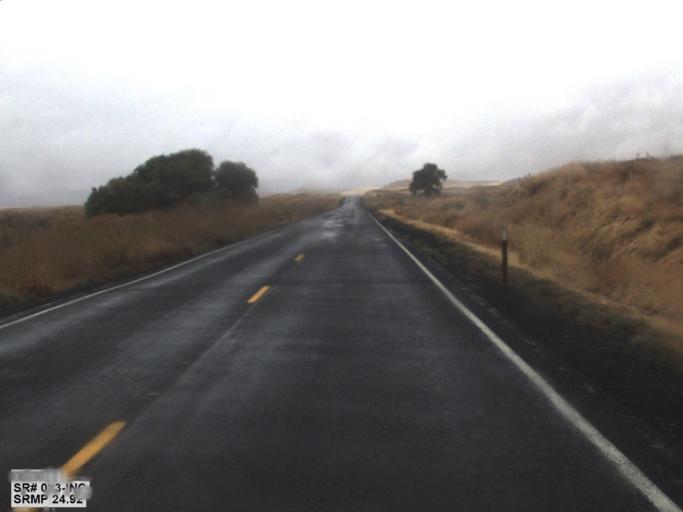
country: US
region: Washington
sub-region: Spokane County
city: Cheney
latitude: 47.1186
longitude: -117.7819
